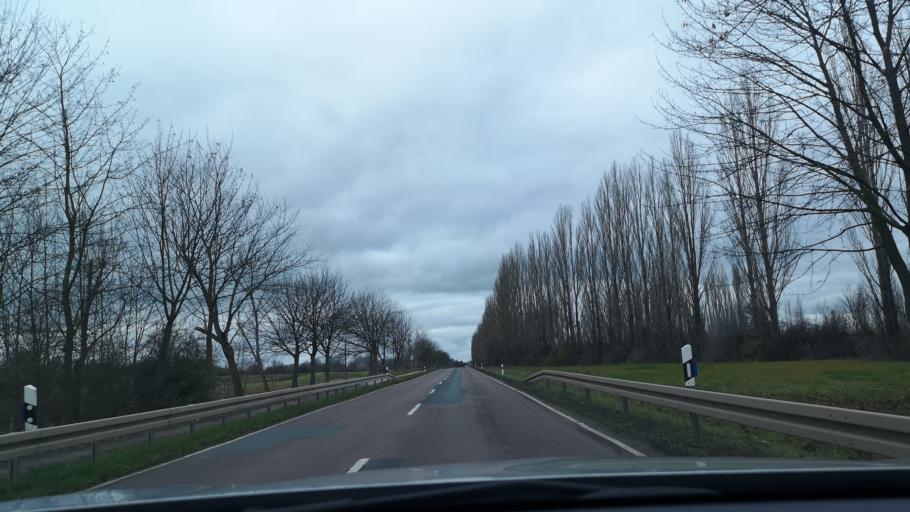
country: DE
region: Saxony-Anhalt
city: Braunsbedra
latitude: 51.2865
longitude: 11.8665
